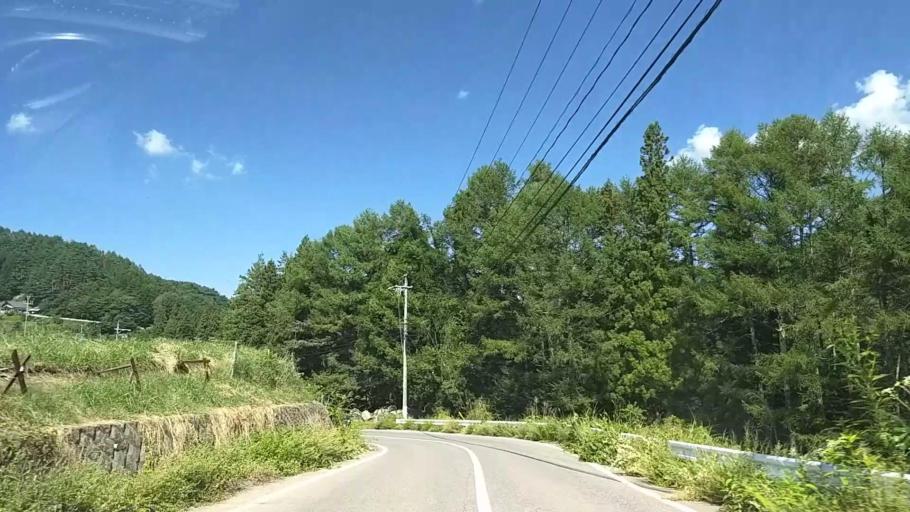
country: JP
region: Nagano
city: Matsumoto
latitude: 36.2044
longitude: 138.0607
